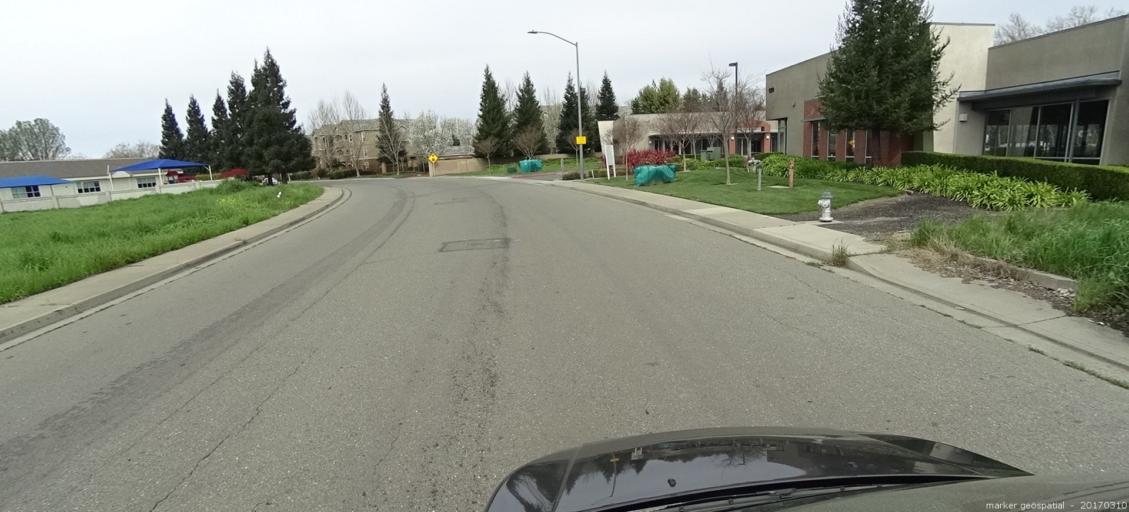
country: US
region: California
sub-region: Sacramento County
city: Parkway
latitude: 38.4921
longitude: -121.5165
